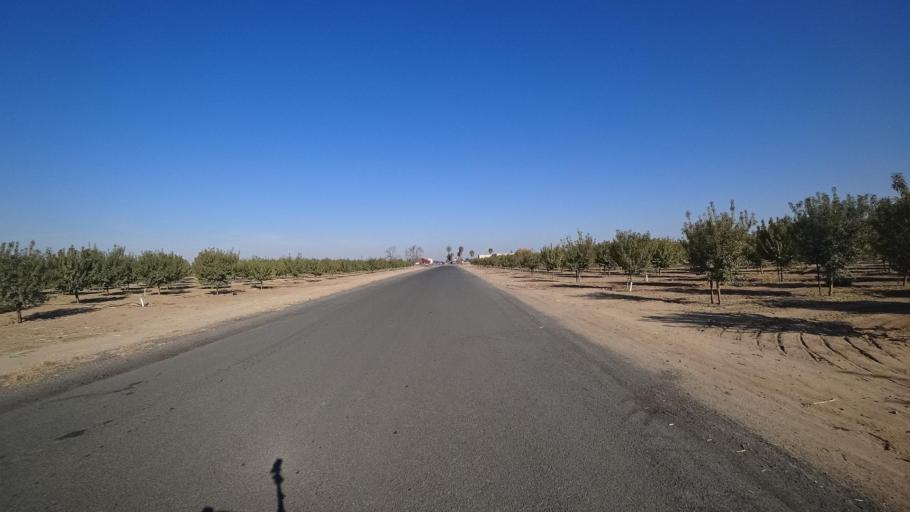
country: US
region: California
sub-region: Kern County
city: Delano
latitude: 35.7581
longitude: -119.2318
